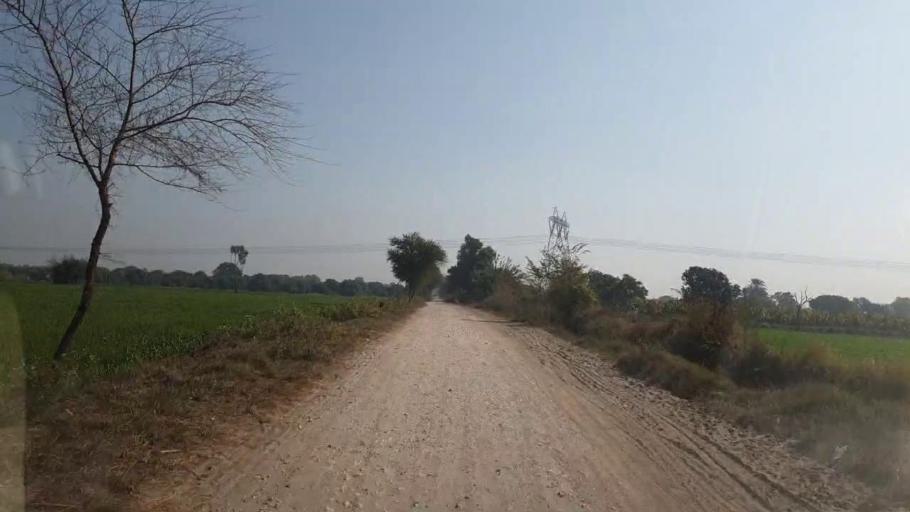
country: PK
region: Sindh
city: Matiari
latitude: 25.5445
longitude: 68.4903
